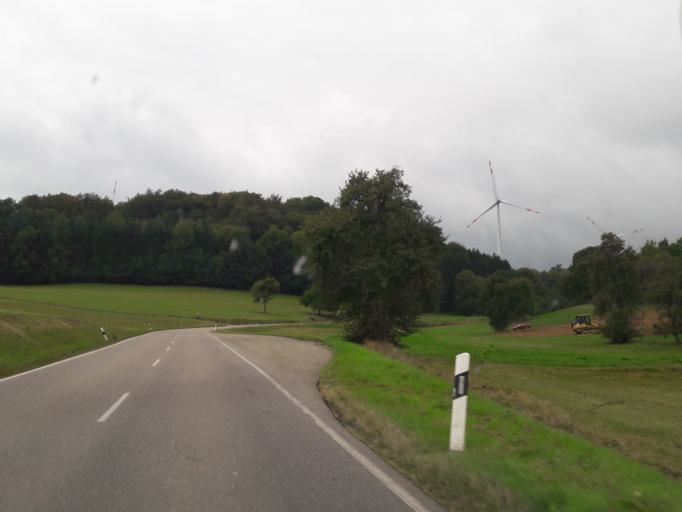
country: DE
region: Baden-Wuerttemberg
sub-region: Regierungsbezirk Stuttgart
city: Widdern
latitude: 49.3053
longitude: 9.4197
